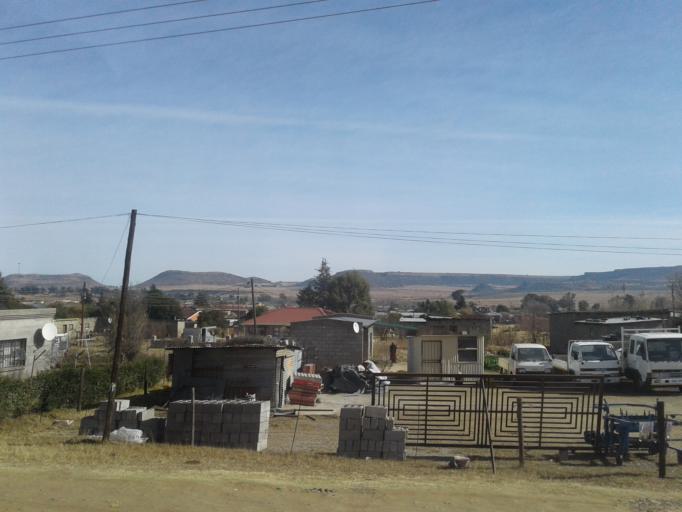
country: LS
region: Maseru
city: Maseru
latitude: -29.2906
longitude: 27.5207
